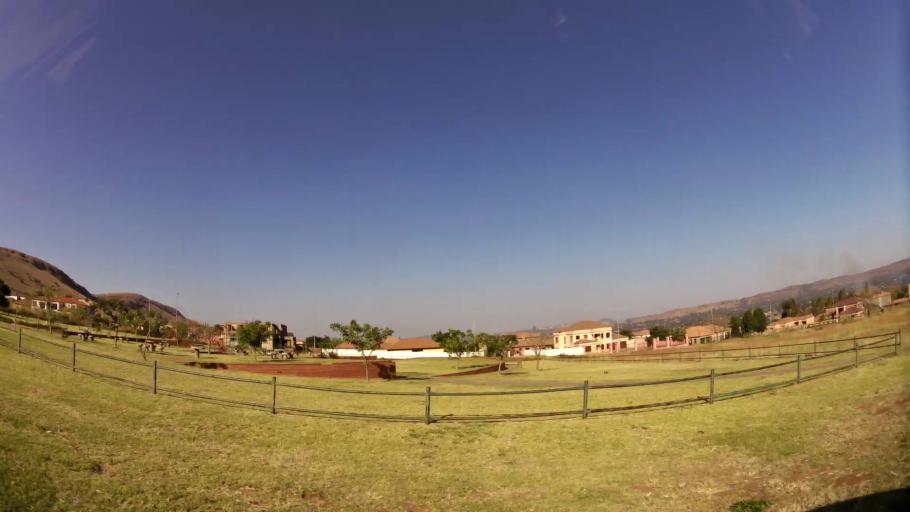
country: ZA
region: Gauteng
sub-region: City of Tshwane Metropolitan Municipality
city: Pretoria
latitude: -25.6933
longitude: 28.1318
